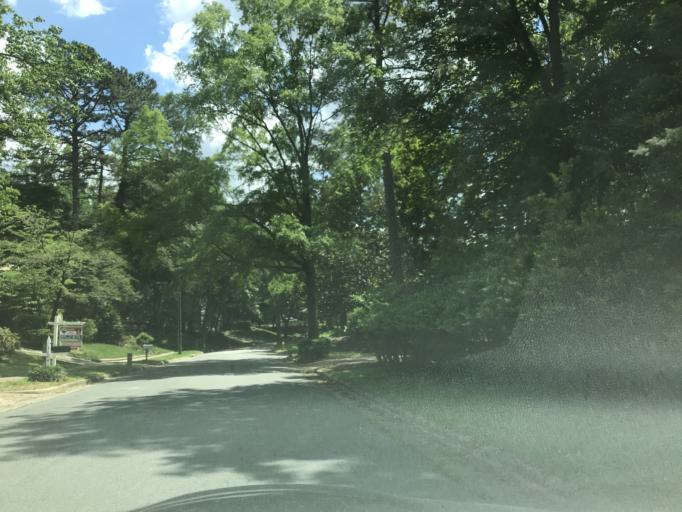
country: US
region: North Carolina
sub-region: Wake County
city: West Raleigh
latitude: 35.8581
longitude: -78.6252
